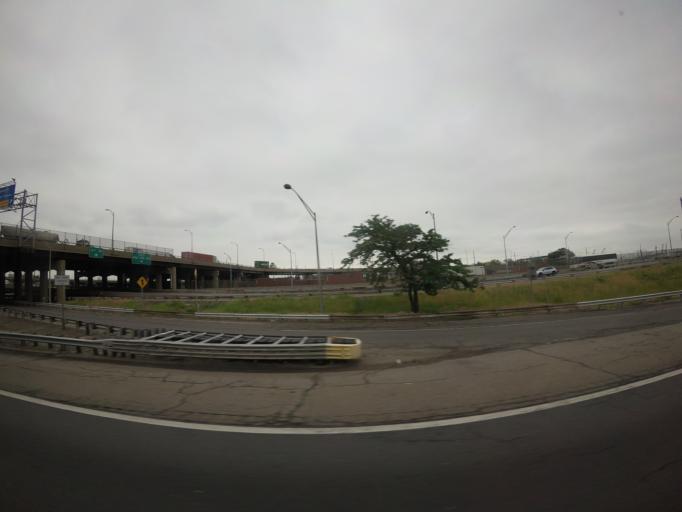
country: US
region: New Jersey
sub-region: Essex County
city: Newark
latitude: 40.7045
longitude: -74.1523
